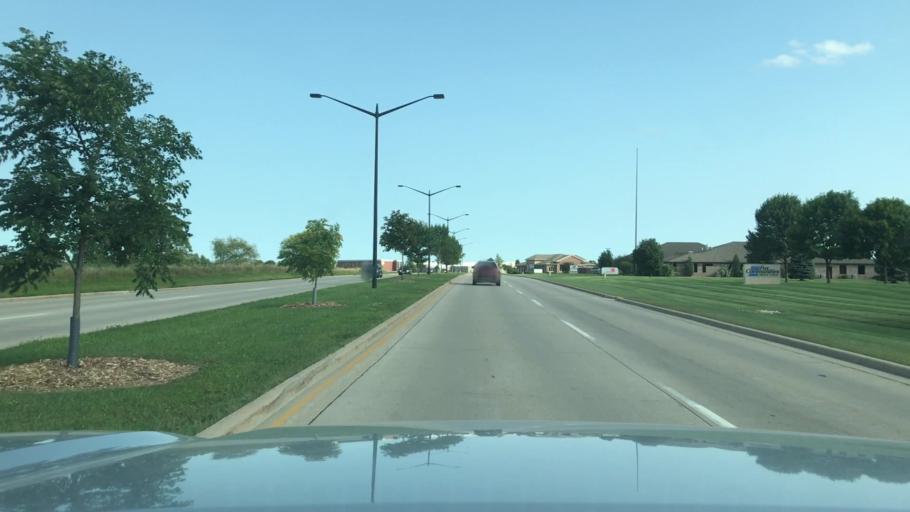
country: US
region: Wisconsin
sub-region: Brown County
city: Bellevue
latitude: 44.4868
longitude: -87.9252
